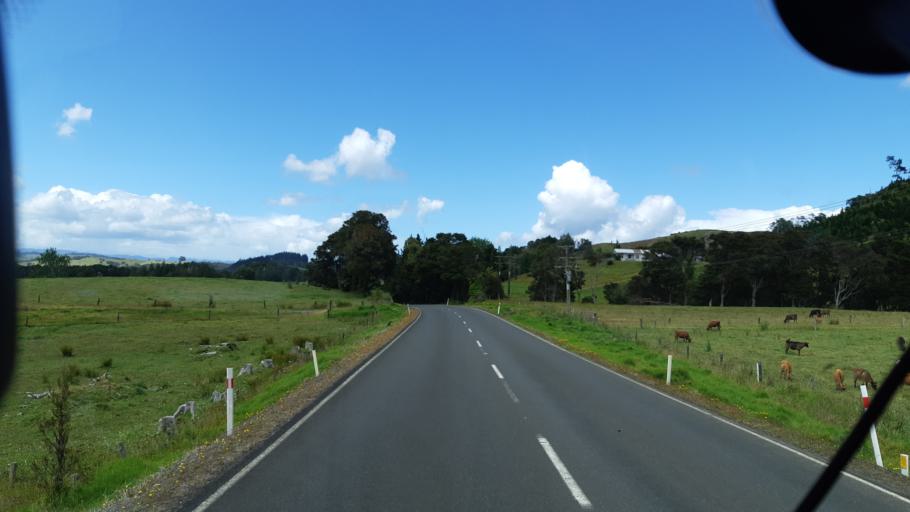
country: NZ
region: Northland
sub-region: Far North District
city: Taipa
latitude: -35.2589
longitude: 173.5284
